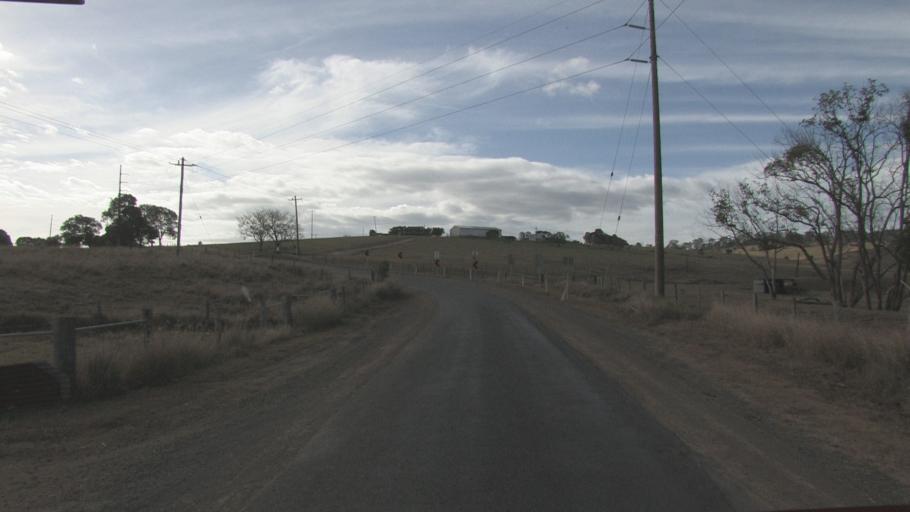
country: AU
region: Queensland
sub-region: Logan
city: Cedar Vale
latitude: -27.9121
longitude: 153.0139
